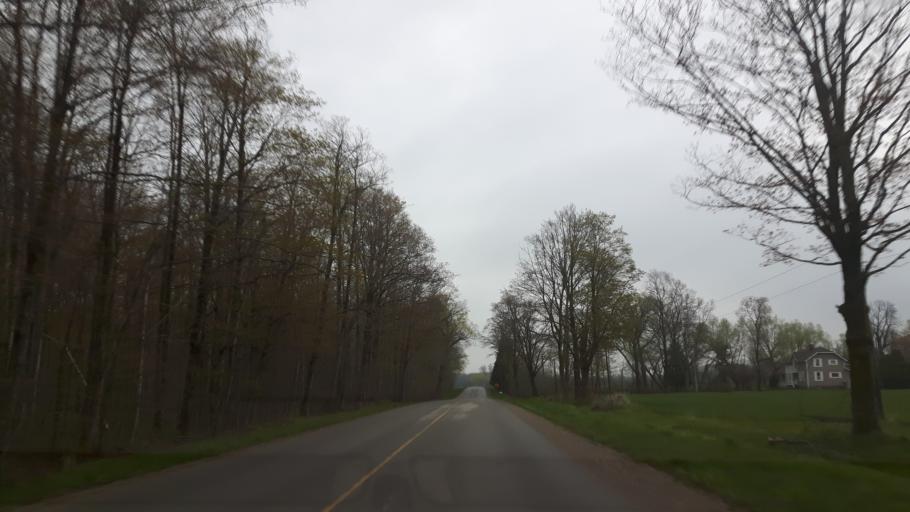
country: CA
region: Ontario
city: Bluewater
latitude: 43.5393
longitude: -81.6744
